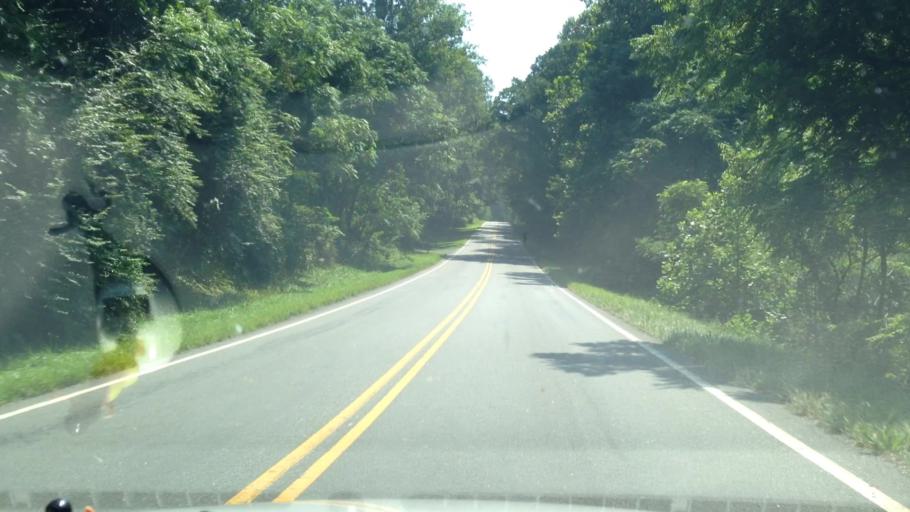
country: US
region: Virginia
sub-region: Patrick County
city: Stuart
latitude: 36.5870
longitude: -80.4024
